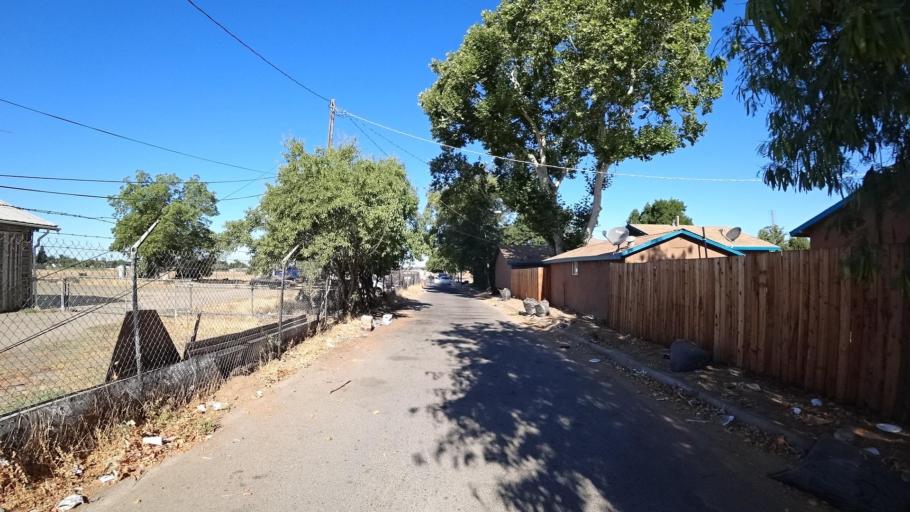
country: US
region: California
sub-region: Fresno County
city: Fresno
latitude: 36.7105
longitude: -119.7914
